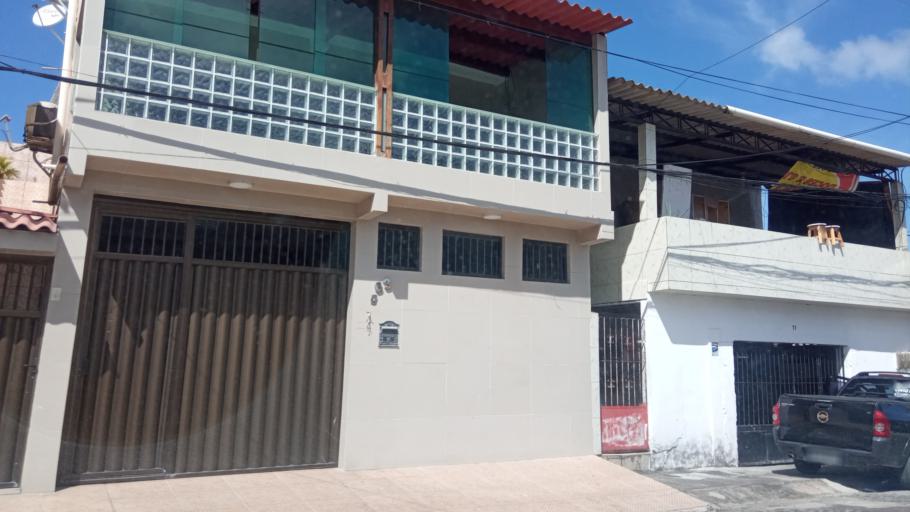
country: BR
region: Pernambuco
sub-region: Jaboatao Dos Guararapes
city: Jaboatao dos Guararapes
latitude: -8.1203
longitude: -34.9463
